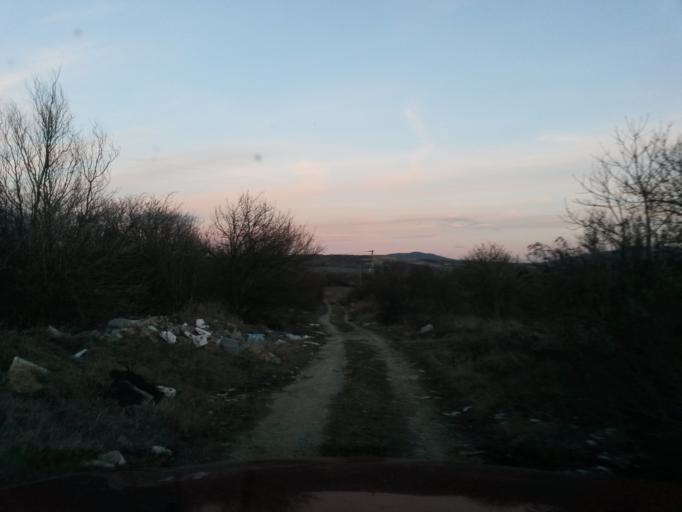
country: SK
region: Kosicky
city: Kosice
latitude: 48.7041
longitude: 21.3251
